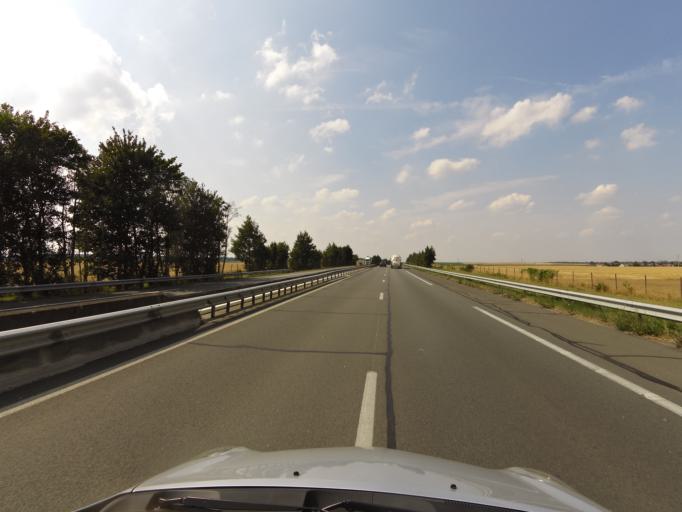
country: FR
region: Picardie
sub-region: Departement de l'Aisne
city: Couvron-et-Aumencourt
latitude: 49.6669
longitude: 3.5259
